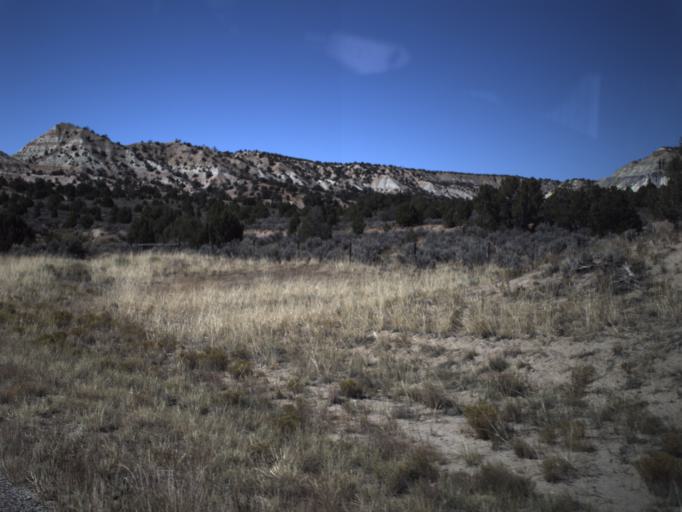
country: US
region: Utah
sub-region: Garfield County
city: Panguitch
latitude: 37.5625
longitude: -112.0323
